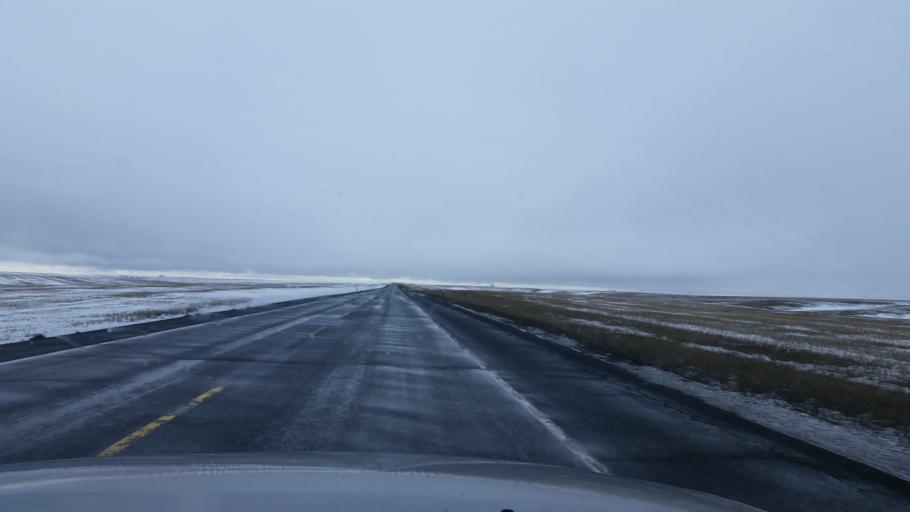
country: US
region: Washington
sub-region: Lincoln County
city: Davenport
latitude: 47.4592
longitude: -118.3066
